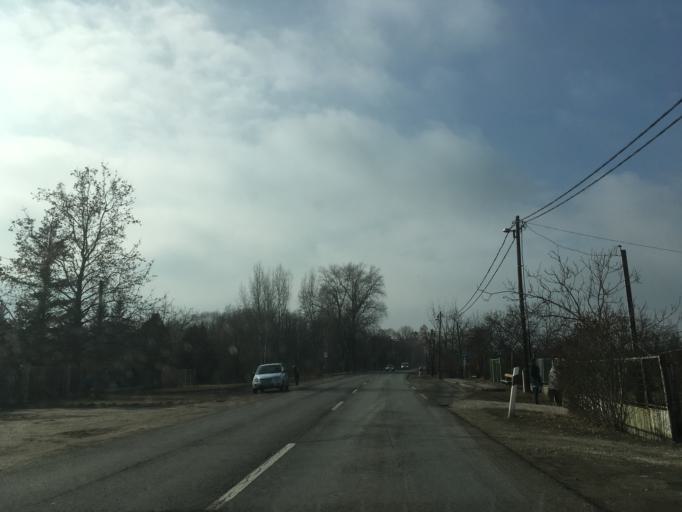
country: HU
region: Komarom-Esztergom
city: Esztergom
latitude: 47.8125
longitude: 18.7818
